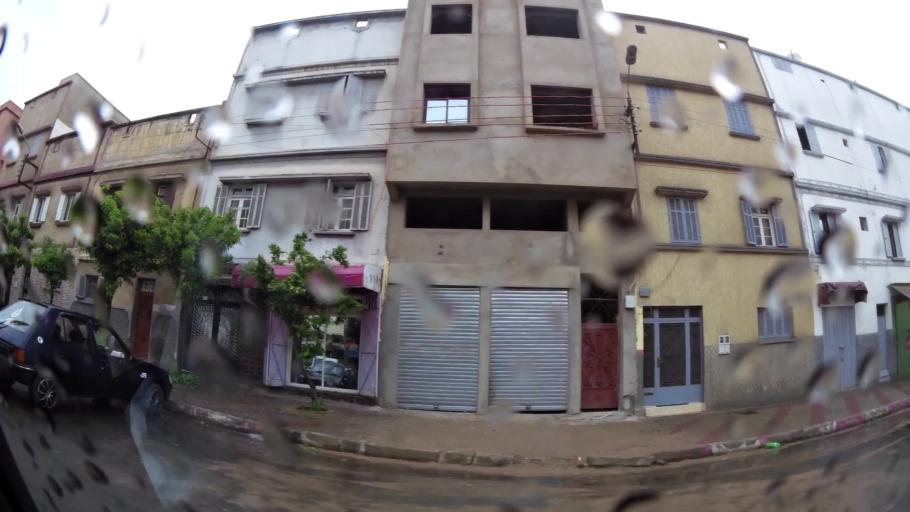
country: MA
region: Grand Casablanca
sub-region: Casablanca
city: Casablanca
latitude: 33.5475
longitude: -7.5791
